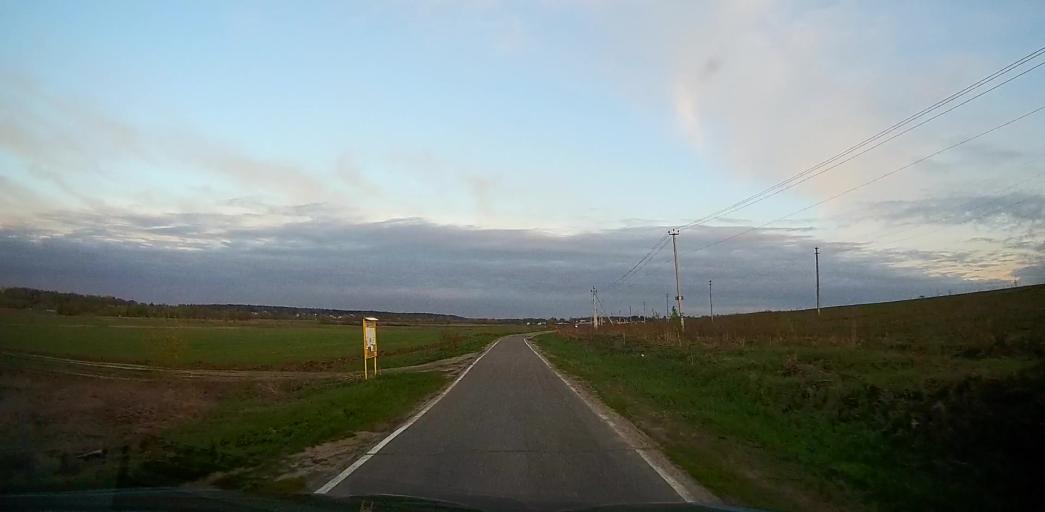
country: RU
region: Moskovskaya
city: Peski
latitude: 55.2258
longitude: 38.7353
